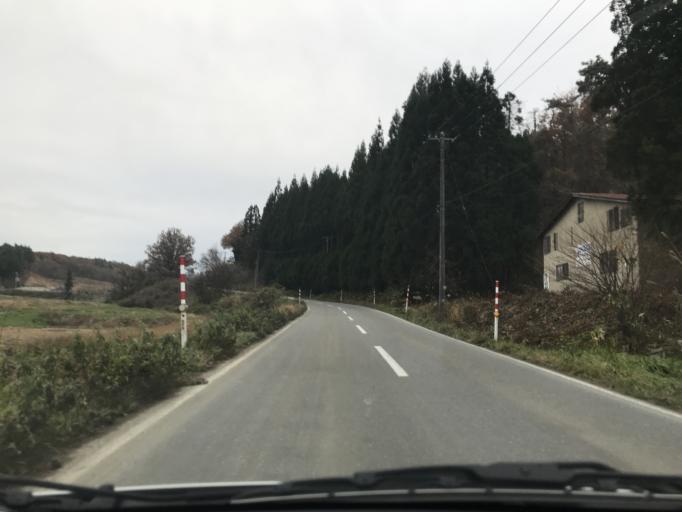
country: JP
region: Iwate
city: Kitakami
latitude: 39.2584
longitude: 141.2660
